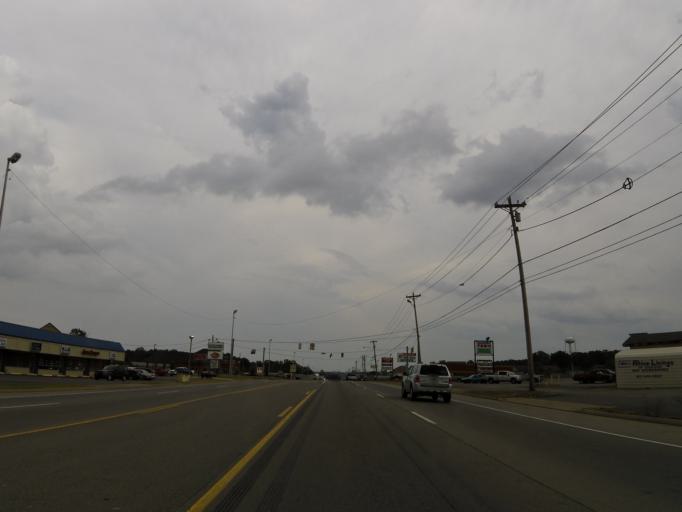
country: US
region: Tennessee
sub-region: Dickson County
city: Burns
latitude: 36.0333
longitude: -87.3528
